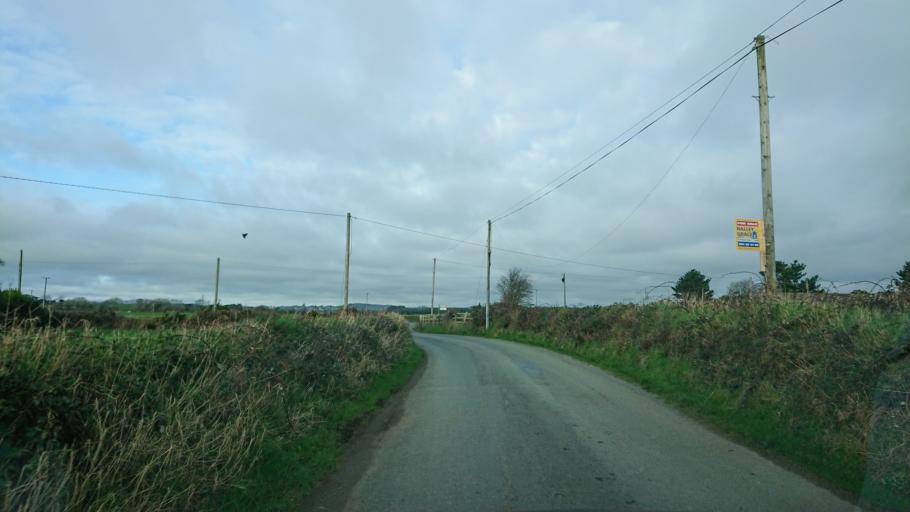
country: IE
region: Munster
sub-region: Waterford
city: Portlaw
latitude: 52.1508
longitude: -7.3094
